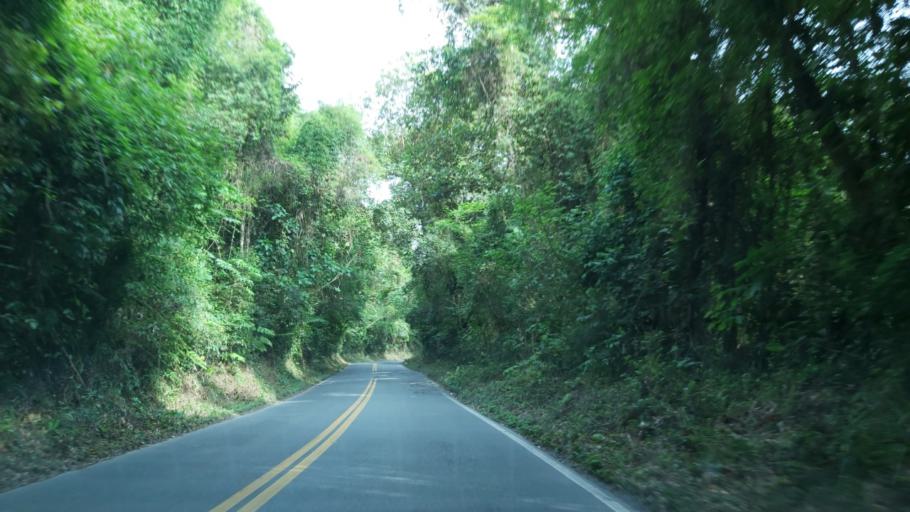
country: BR
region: Sao Paulo
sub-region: Juquia
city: Juquia
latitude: -24.1074
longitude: -47.6244
